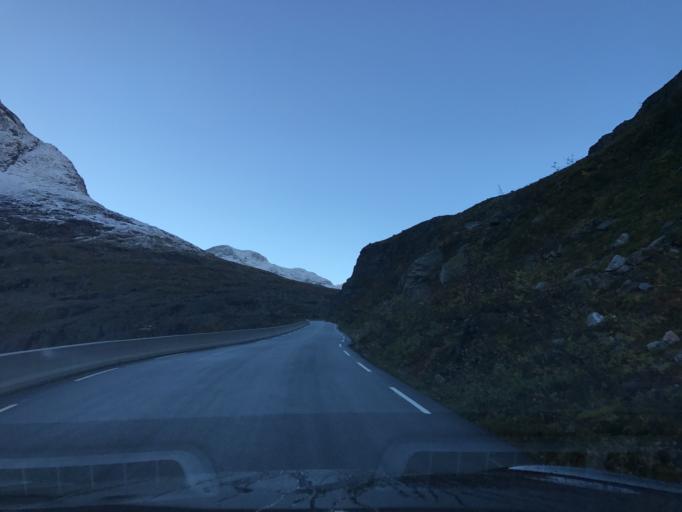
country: NO
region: More og Romsdal
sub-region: Rauma
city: Andalsnes
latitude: 62.4618
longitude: 7.6659
